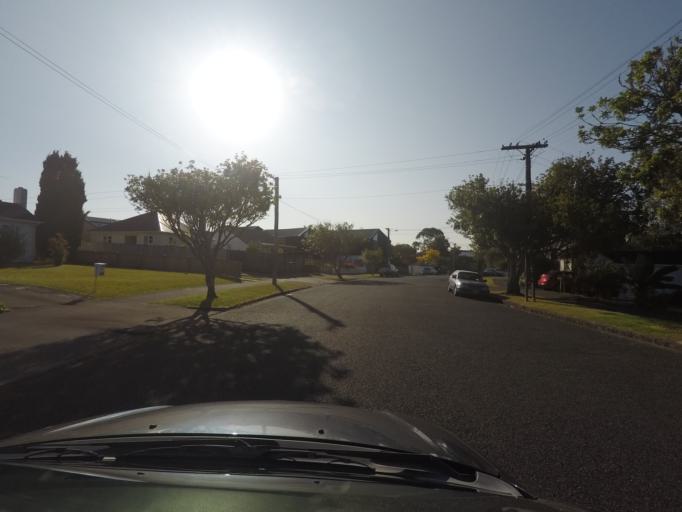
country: NZ
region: Auckland
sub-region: Auckland
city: Rosebank
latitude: -36.8646
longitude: 174.7148
